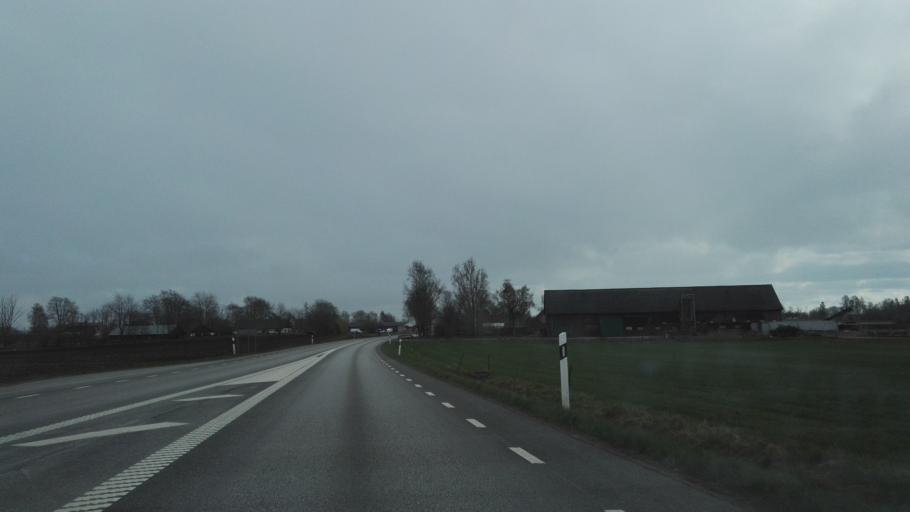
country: SE
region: Skane
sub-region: Horby Kommun
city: Hoerby
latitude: 55.7902
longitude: 13.6761
